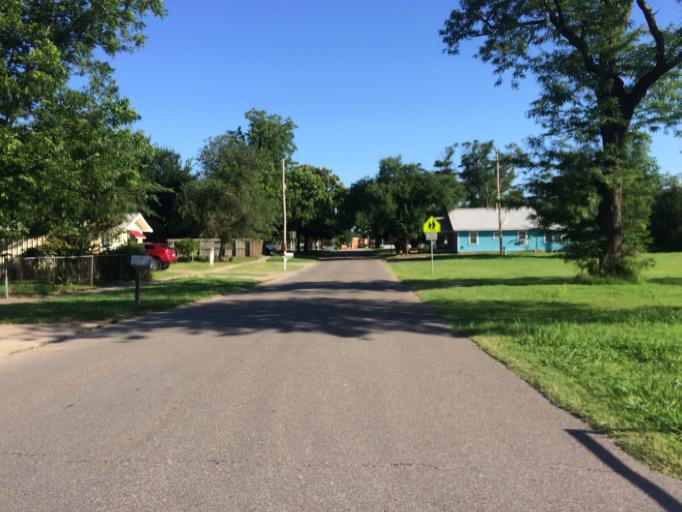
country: US
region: Oklahoma
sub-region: Cleveland County
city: Norman
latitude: 35.2241
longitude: -97.4331
